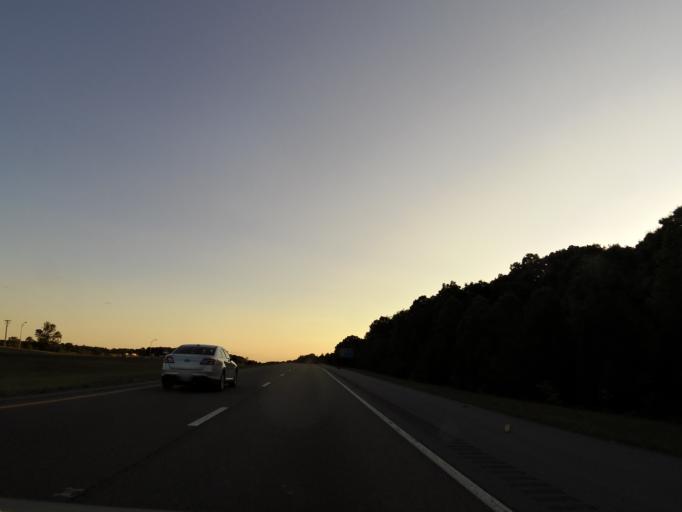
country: US
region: Tennessee
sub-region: Hawkins County
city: Surgoinsville
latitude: 36.3379
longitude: -82.8067
